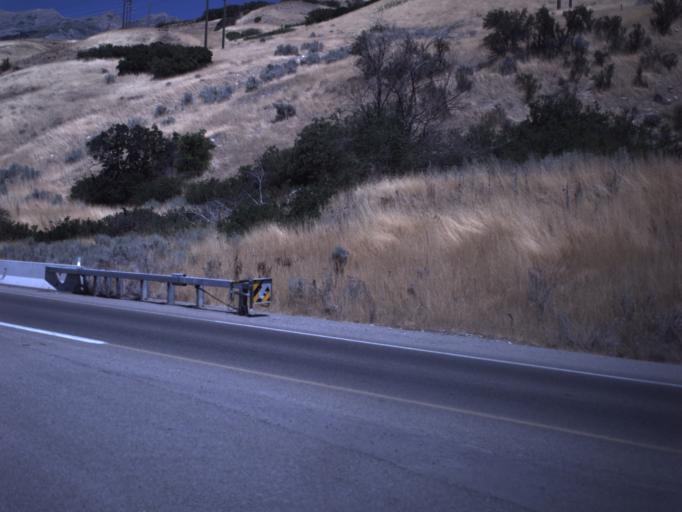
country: US
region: Utah
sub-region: Utah County
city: Orem
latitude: 40.3085
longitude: -111.6553
